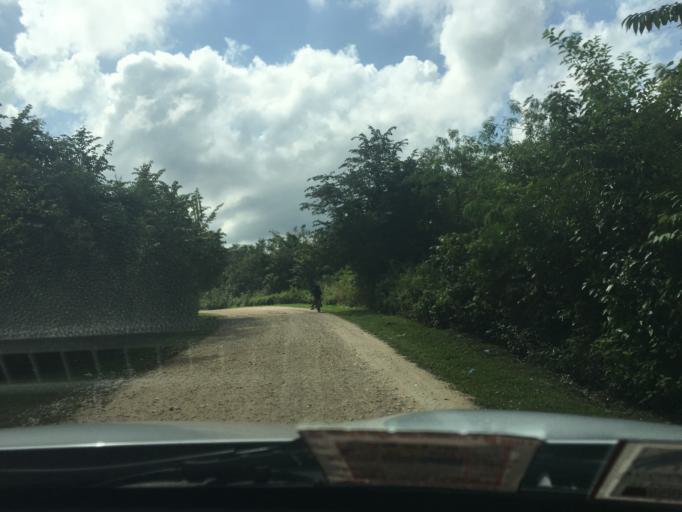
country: BZ
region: Cayo
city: Belmopan
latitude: 17.2493
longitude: -88.7928
